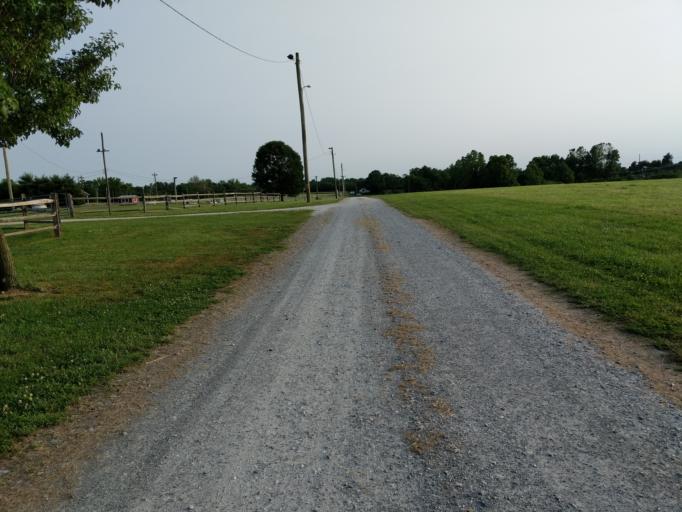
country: US
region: New Jersey
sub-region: Salem County
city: Woodstown
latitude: 39.6688
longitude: -75.3800
